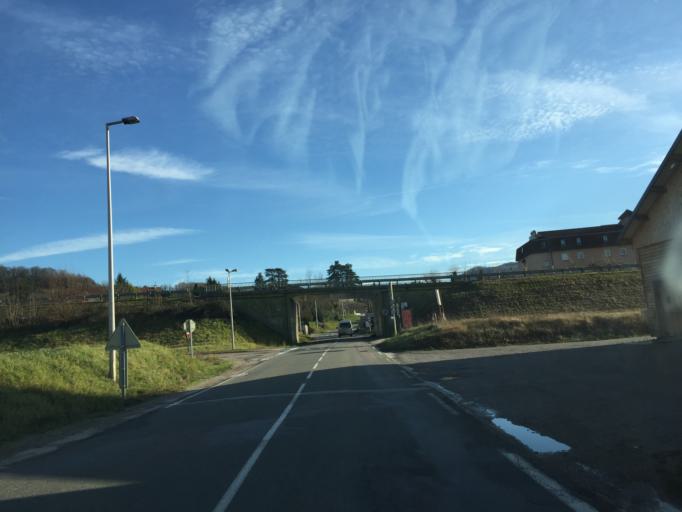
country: FR
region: Franche-Comte
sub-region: Departement du Jura
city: Arbois
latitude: 46.9131
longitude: 5.7678
